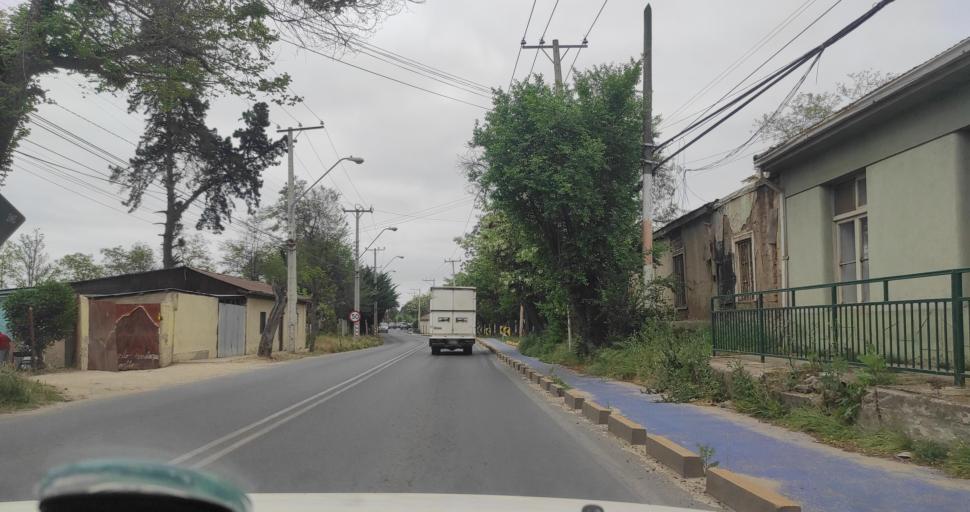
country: CL
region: Valparaiso
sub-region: Provincia de Marga Marga
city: Limache
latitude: -32.9940
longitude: -71.2427
